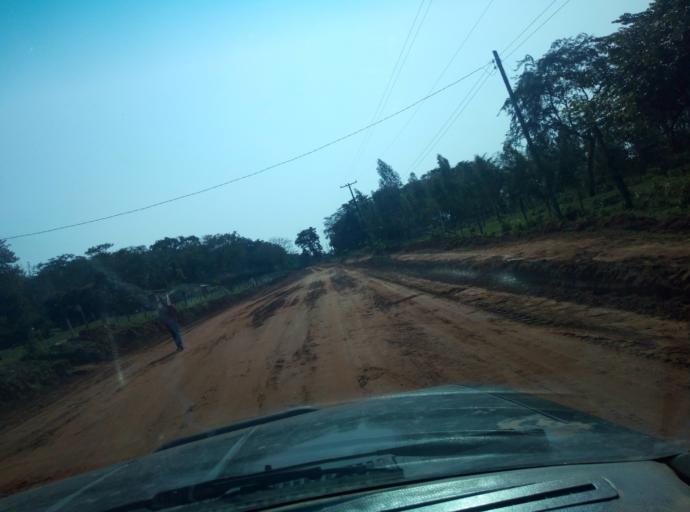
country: PY
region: Caaguazu
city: Carayao
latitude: -25.3081
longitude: -56.3253
